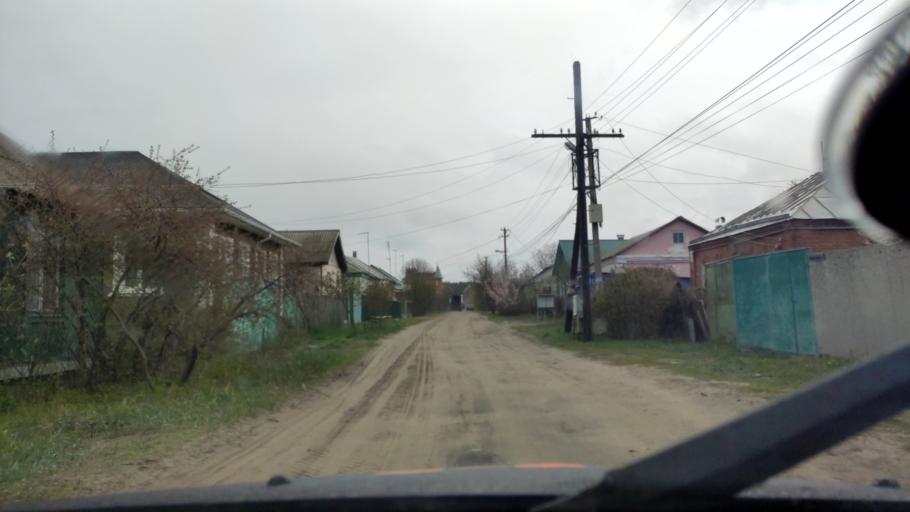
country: RU
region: Voronezj
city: Somovo
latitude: 51.7405
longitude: 39.2627
